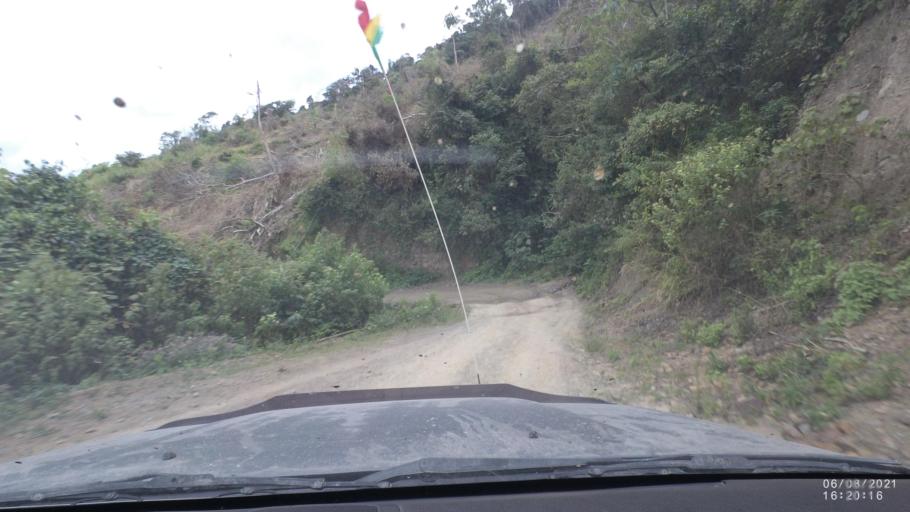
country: BO
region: La Paz
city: Quime
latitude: -16.5460
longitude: -66.7465
